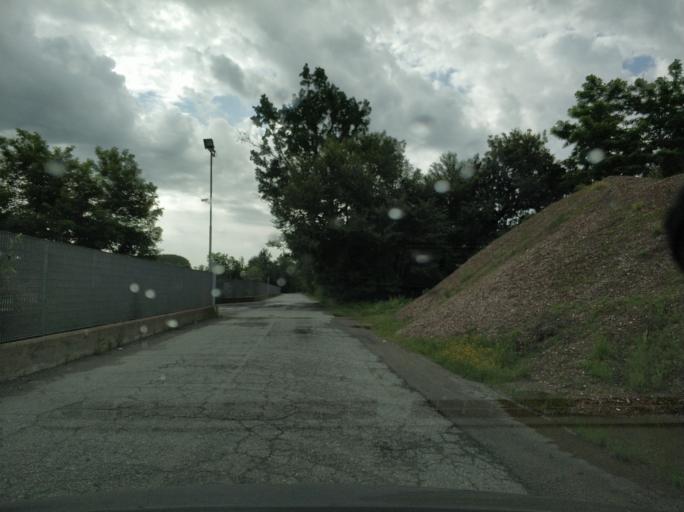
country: IT
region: Piedmont
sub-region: Provincia di Torino
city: Robassomero
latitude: 45.1890
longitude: 7.6025
